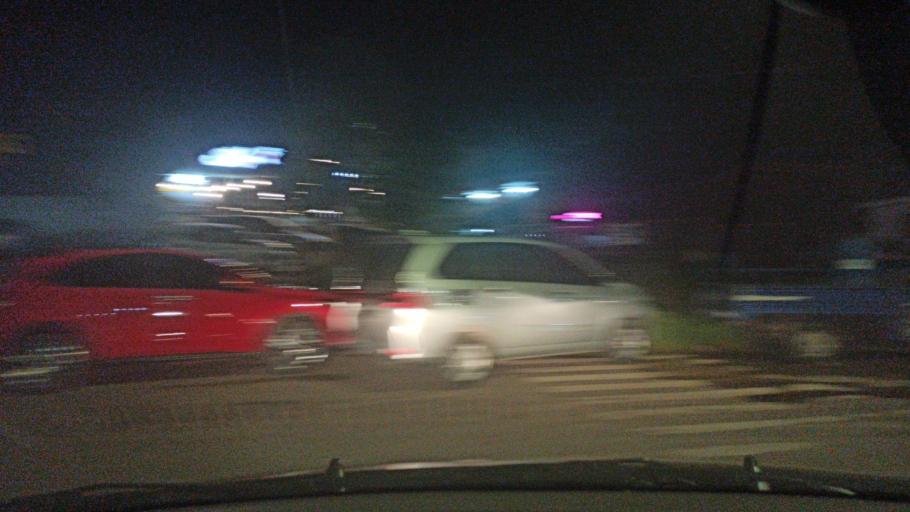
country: ID
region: South Sumatra
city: Palembang
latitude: -2.9527
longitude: 104.7549
